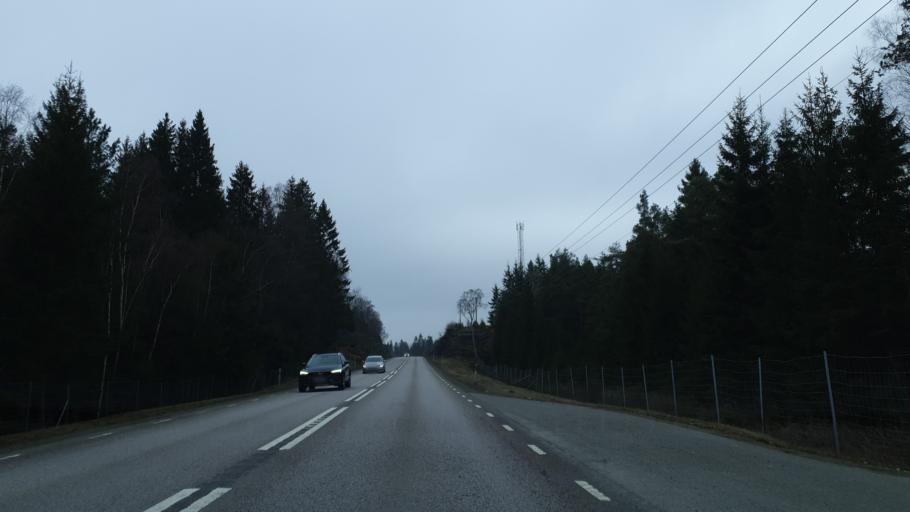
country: SE
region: Vaestra Goetaland
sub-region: Harryda Kommun
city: Hindas
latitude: 57.6489
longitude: 12.4024
